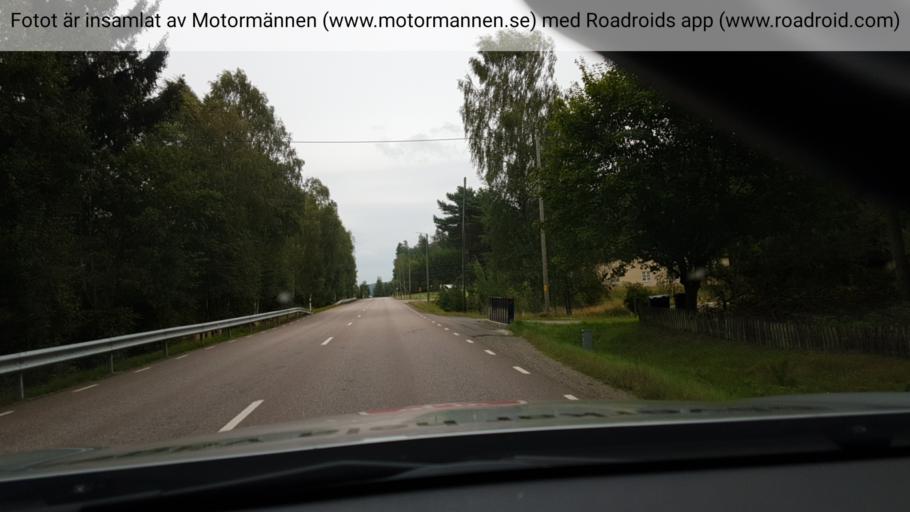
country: SE
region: Vaestra Goetaland
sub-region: Harryda Kommun
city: Landvetter
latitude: 57.6062
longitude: 12.2500
